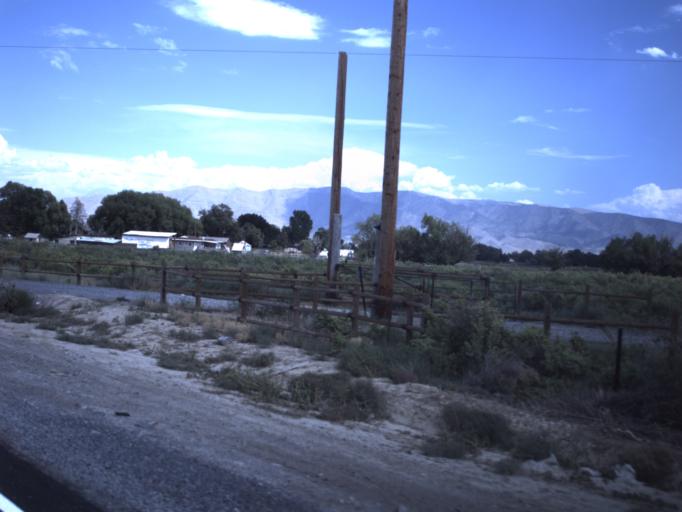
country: US
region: Utah
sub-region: Utah County
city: Eagle Mountain
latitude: 40.2593
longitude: -112.0968
